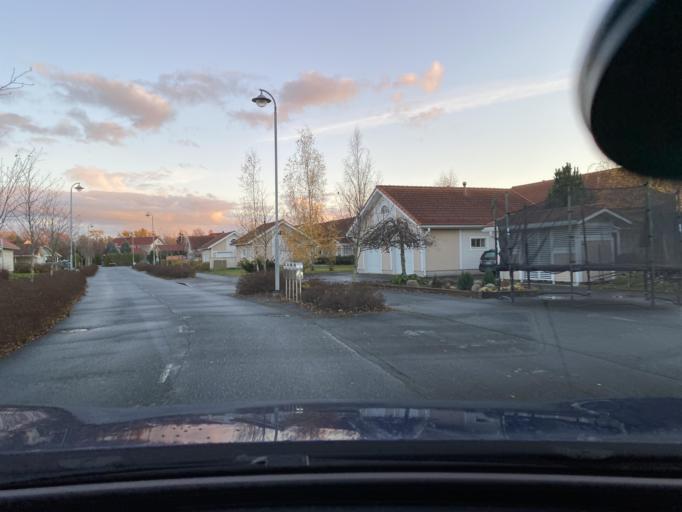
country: FI
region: Satakunta
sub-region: Pori
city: Huittinen
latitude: 61.1813
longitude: 22.7038
